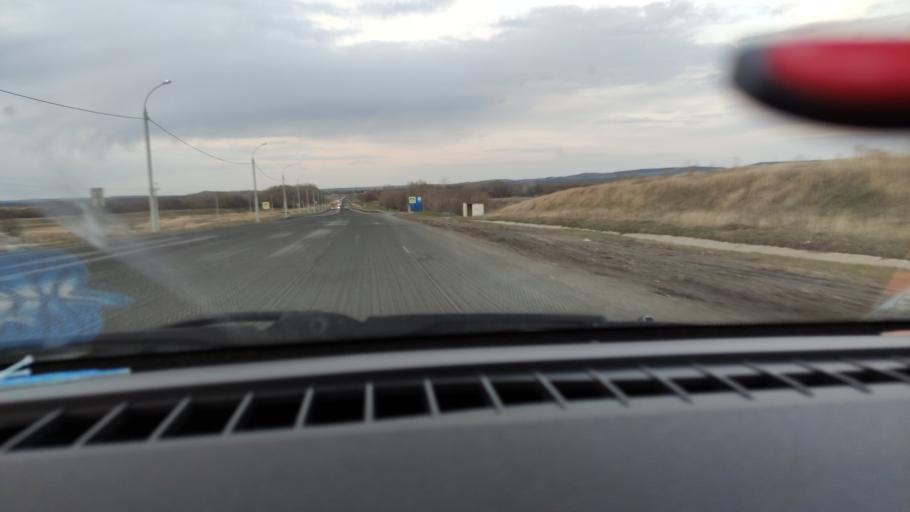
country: RU
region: Saratov
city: Yelshanka
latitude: 51.8207
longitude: 46.2157
